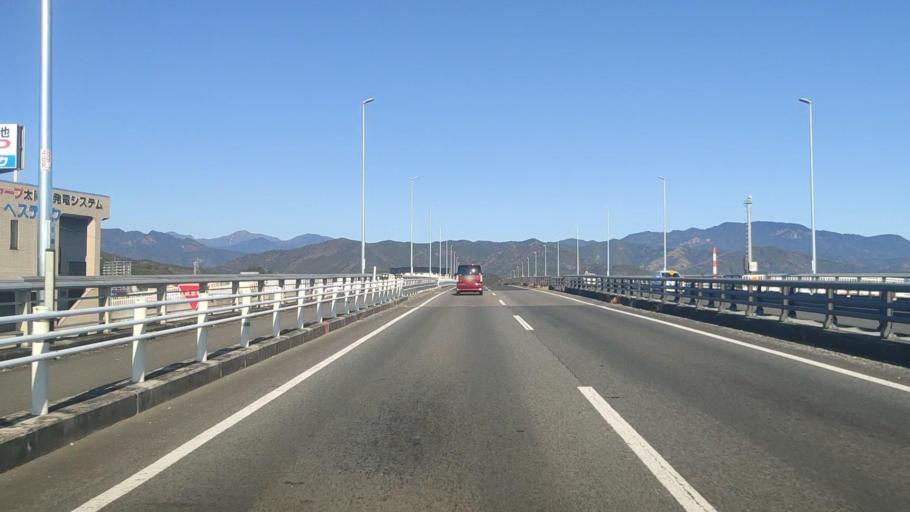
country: JP
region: Miyazaki
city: Nobeoka
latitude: 32.5813
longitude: 131.6811
